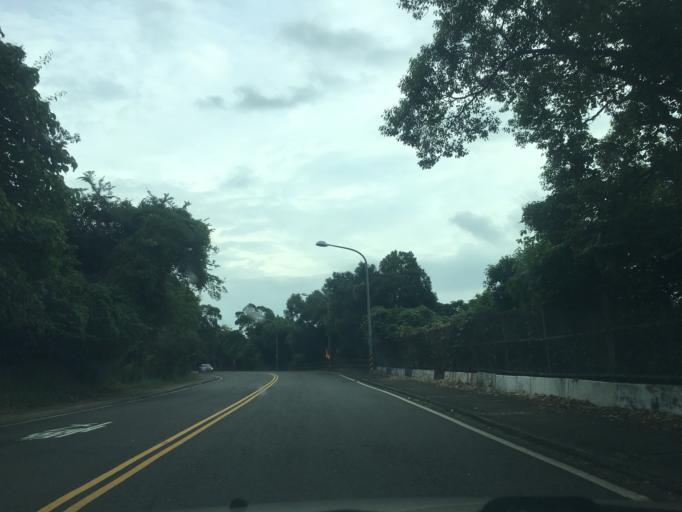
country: TW
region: Taiwan
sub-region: Changhua
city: Chang-hua
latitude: 24.0648
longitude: 120.5700
